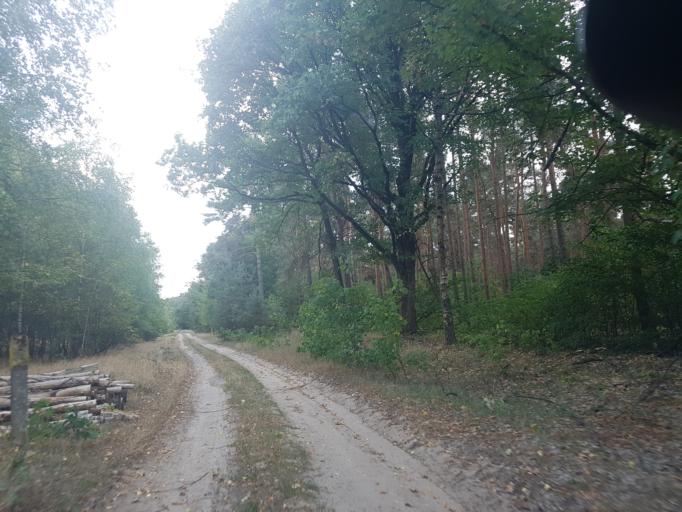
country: DE
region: Brandenburg
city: Treuenbrietzen
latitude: 52.0438
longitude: 12.8581
